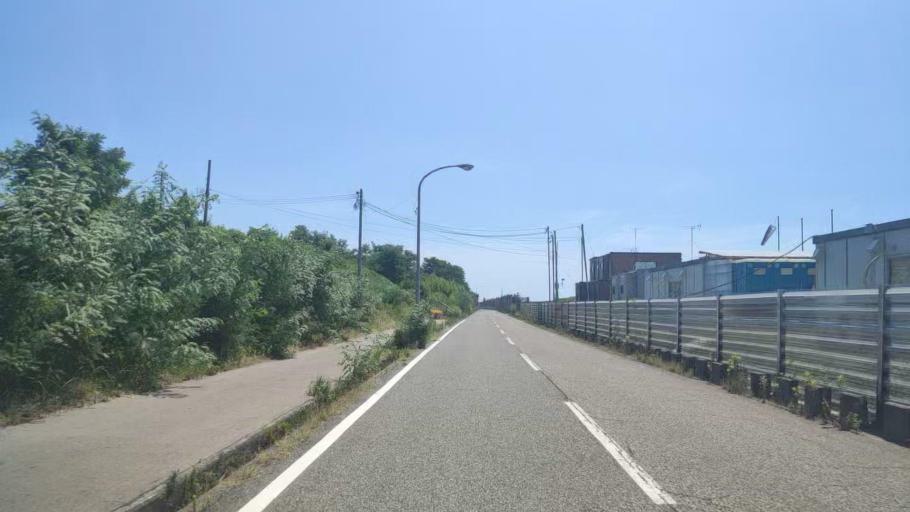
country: JP
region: Ishikawa
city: Kanazawa-shi
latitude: 36.6084
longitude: 136.5944
